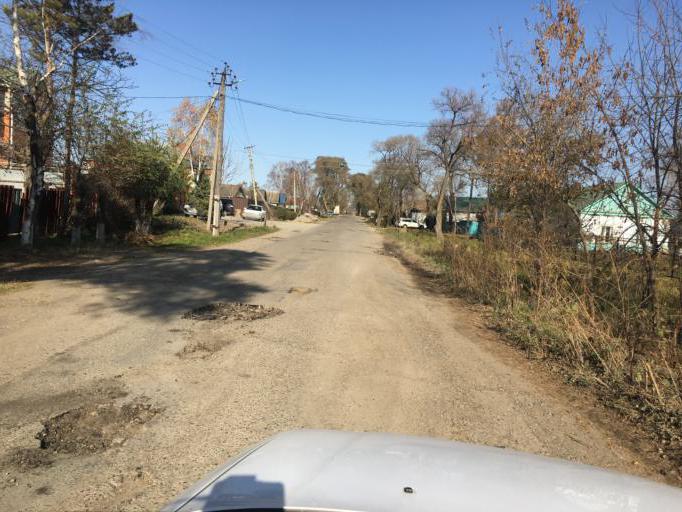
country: RU
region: Primorskiy
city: Dal'nerechensk
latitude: 45.9236
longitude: 133.7182
